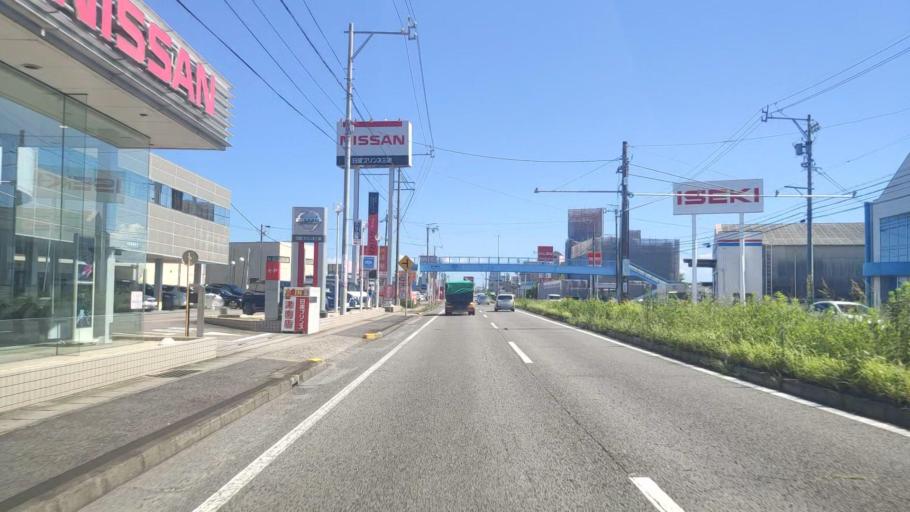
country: JP
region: Mie
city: Tsu-shi
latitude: 34.6955
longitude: 136.5095
